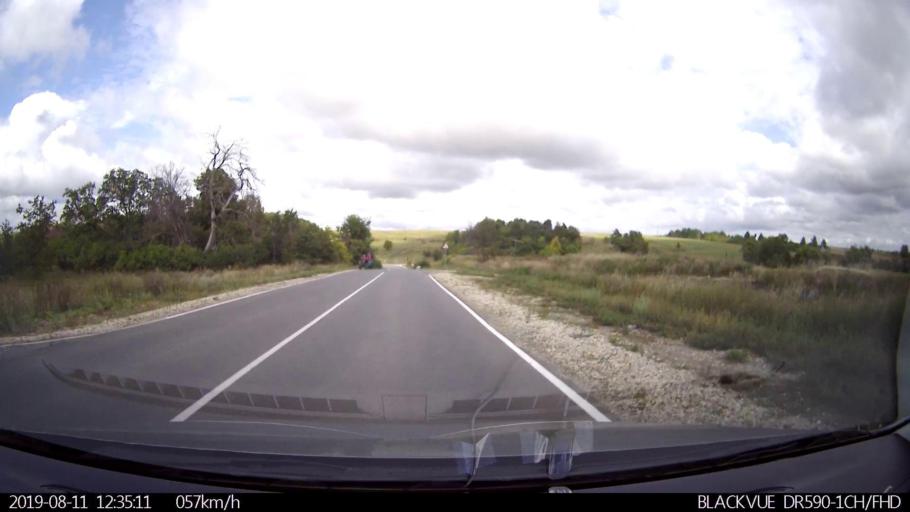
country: RU
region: Ulyanovsk
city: Ignatovka
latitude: 53.8227
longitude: 47.8346
